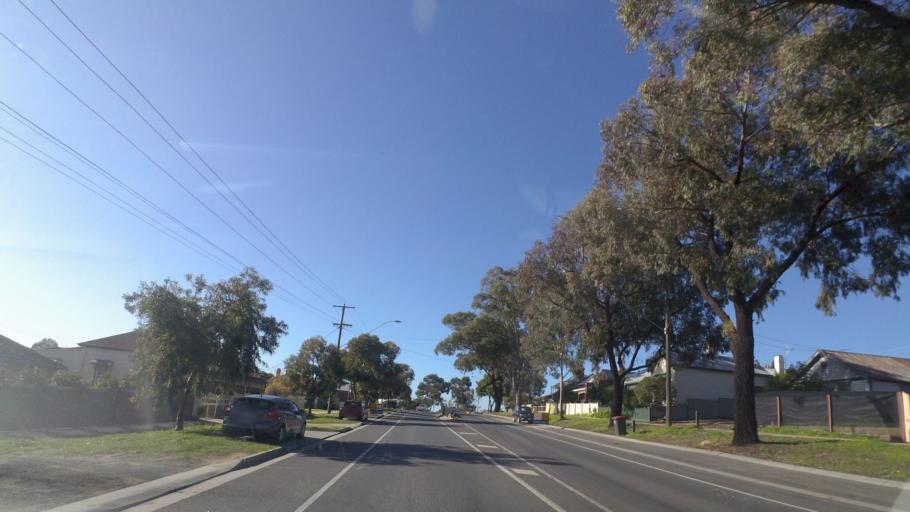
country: AU
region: Victoria
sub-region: Greater Bendigo
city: Quarry Hill
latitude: -36.7704
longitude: 144.2793
